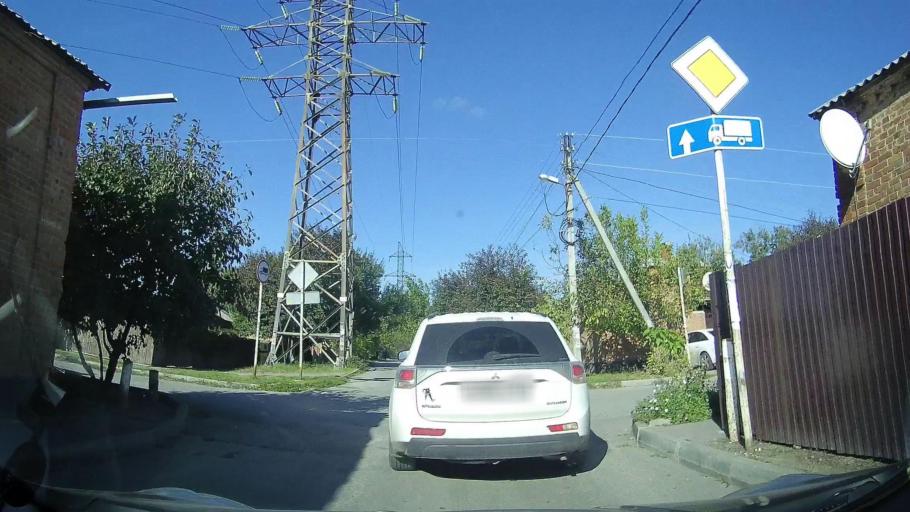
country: RU
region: Rostov
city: Rostov-na-Donu
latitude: 47.2388
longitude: 39.6727
